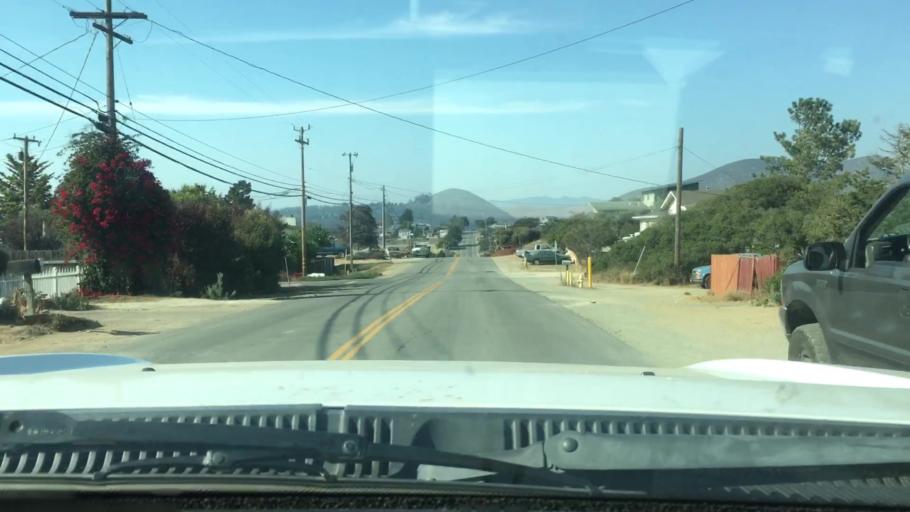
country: US
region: California
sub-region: San Luis Obispo County
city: Los Osos
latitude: 35.3221
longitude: -120.8311
